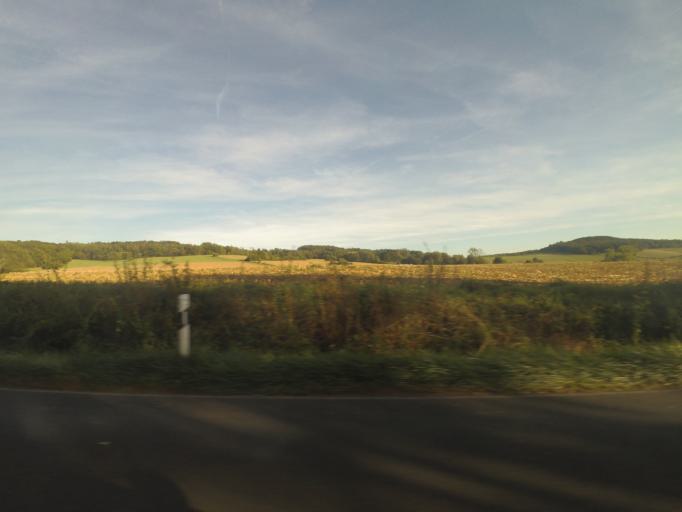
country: DE
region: Hesse
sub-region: Regierungsbezirk Darmstadt
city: Bad Soden-Salmunster
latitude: 50.3222
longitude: 9.3811
